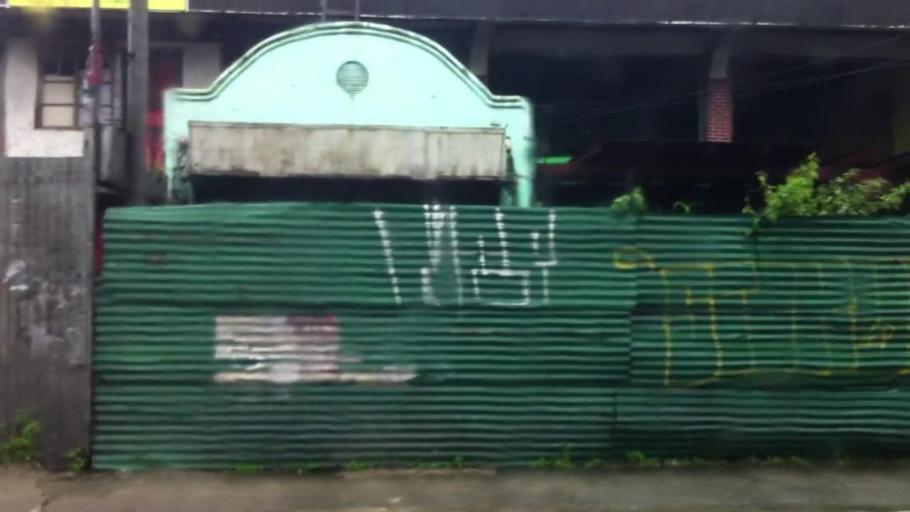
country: PH
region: Cordillera
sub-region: Province of Benguet
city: La Trinidad
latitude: 16.4448
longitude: 120.5916
